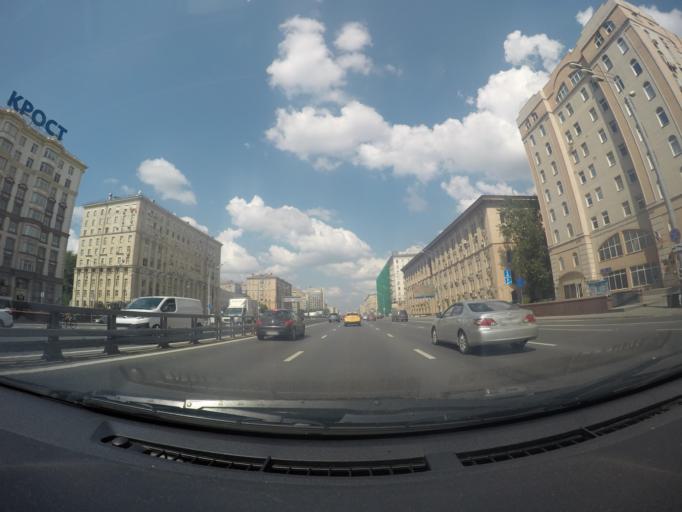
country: RU
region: Moscow
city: Mar'ina Roshcha
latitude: 55.8020
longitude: 37.6359
